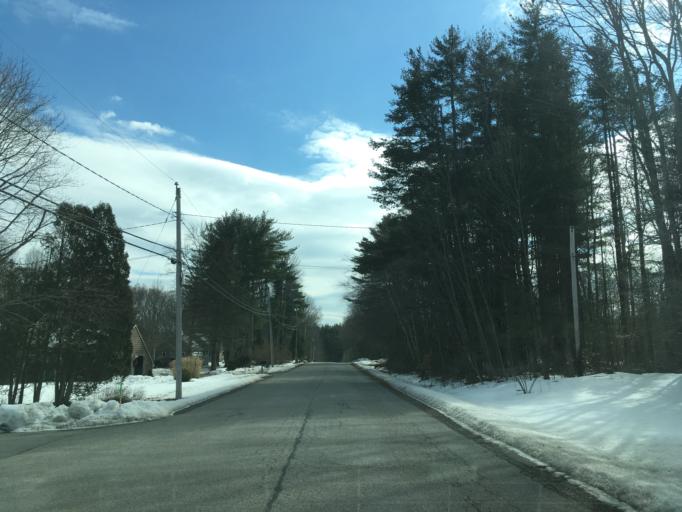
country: US
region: New Hampshire
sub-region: Rockingham County
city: Exeter
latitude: 42.9871
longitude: -70.8903
